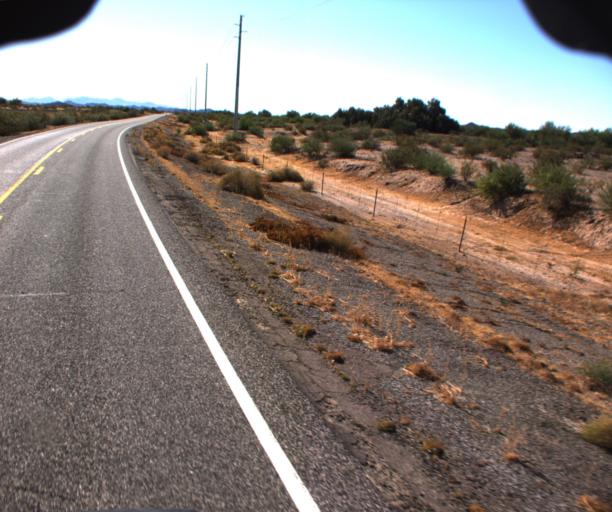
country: US
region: Arizona
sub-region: La Paz County
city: Cienega Springs
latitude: 33.9909
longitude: -114.0796
